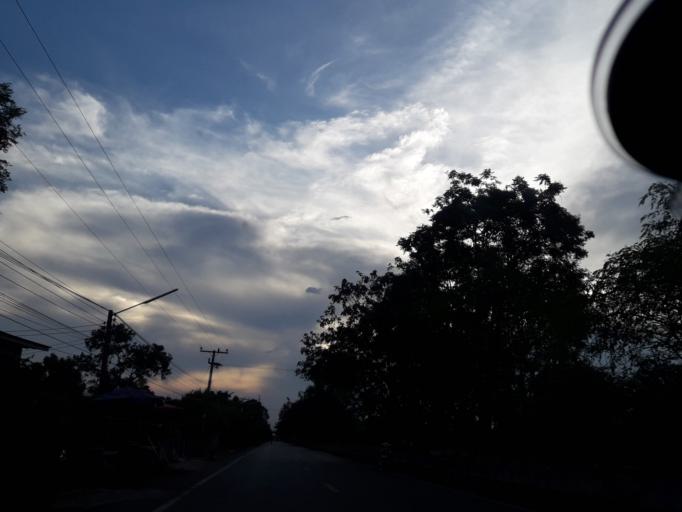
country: TH
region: Sara Buri
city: Nong Khae
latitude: 14.2665
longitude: 100.8720
